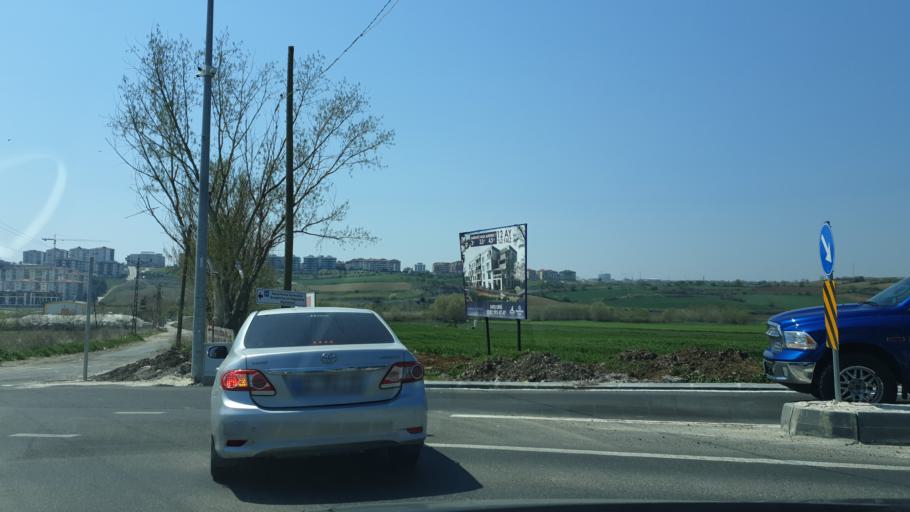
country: TR
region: Tekirdag
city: Tekirdag
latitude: 40.9936
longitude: 27.5771
